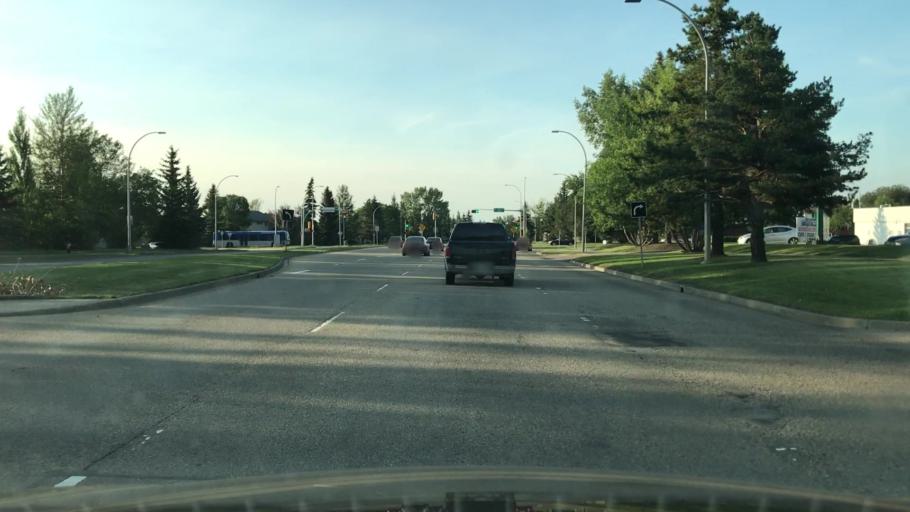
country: CA
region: Alberta
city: Beaumont
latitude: 53.4445
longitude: -113.4190
